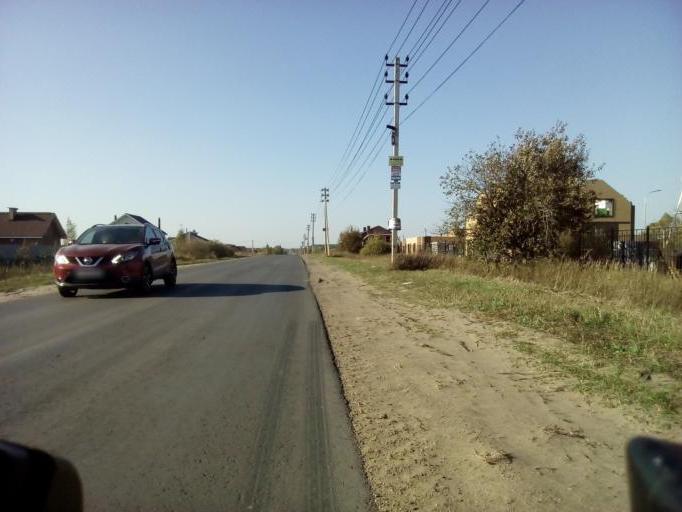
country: RU
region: Moskovskaya
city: Ramenskoye
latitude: 55.5655
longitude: 38.3008
